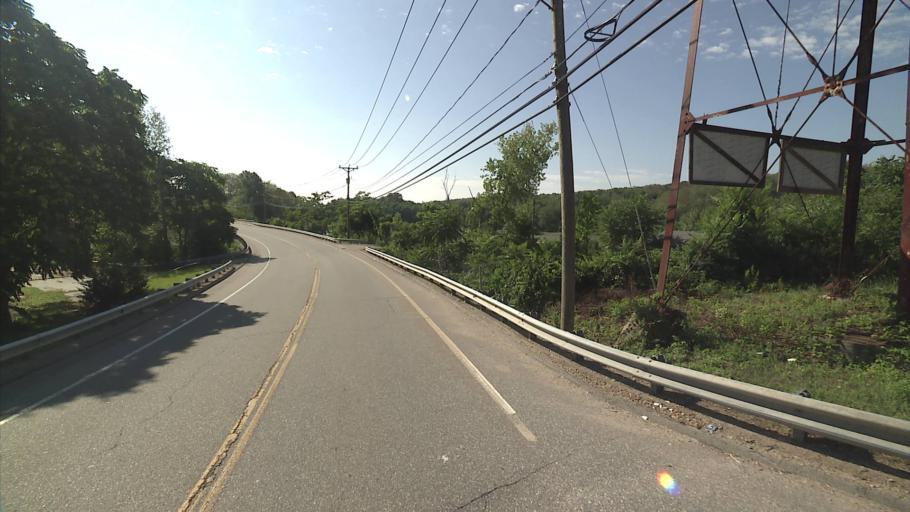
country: US
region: Connecticut
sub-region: New London County
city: Oxoboxo River
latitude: 41.4564
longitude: -72.1424
